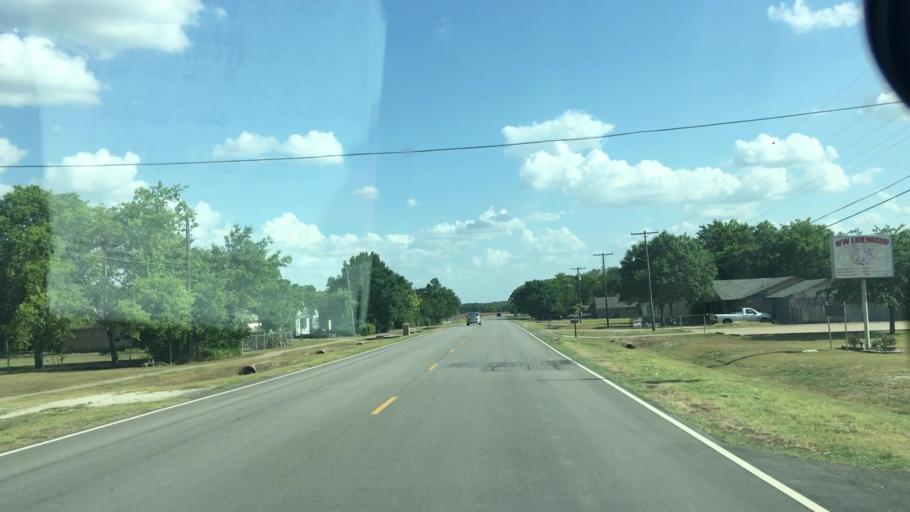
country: US
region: Texas
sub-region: Dallas County
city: Lancaster
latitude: 32.5979
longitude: -96.7479
